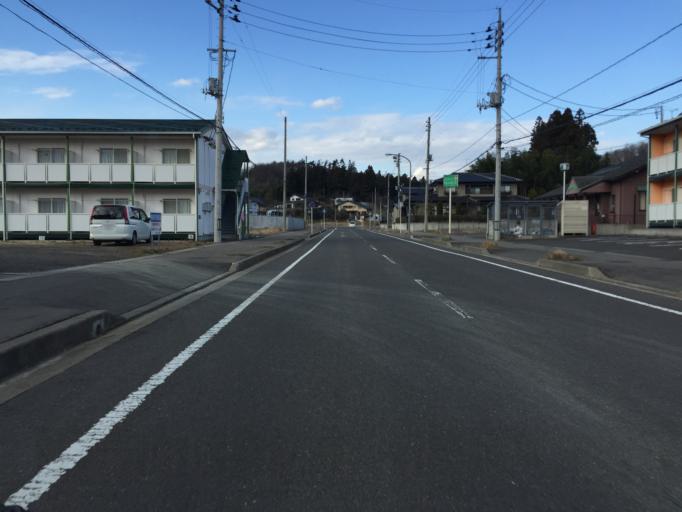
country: JP
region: Fukushima
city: Fukushima-shi
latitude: 37.6816
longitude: 140.4521
